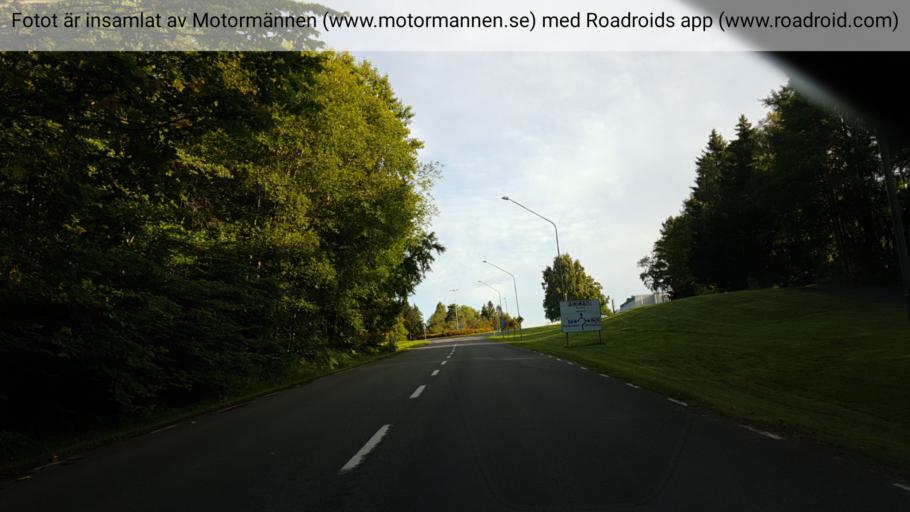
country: SE
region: Vaestra Goetaland
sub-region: Skovde Kommun
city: Skoevde
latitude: 58.3994
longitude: 13.8180
